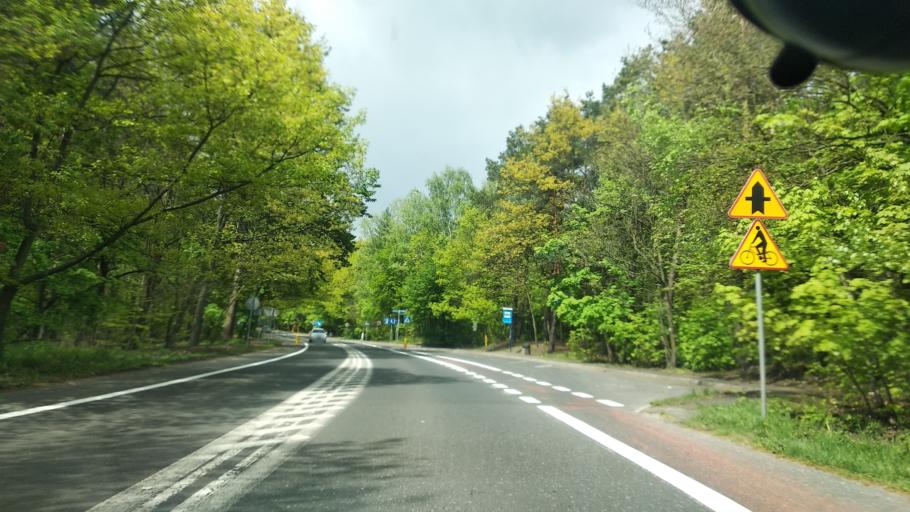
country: PL
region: Silesian Voivodeship
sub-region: Swietochlowice
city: Swietochlowice
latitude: 50.2337
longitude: 18.9146
